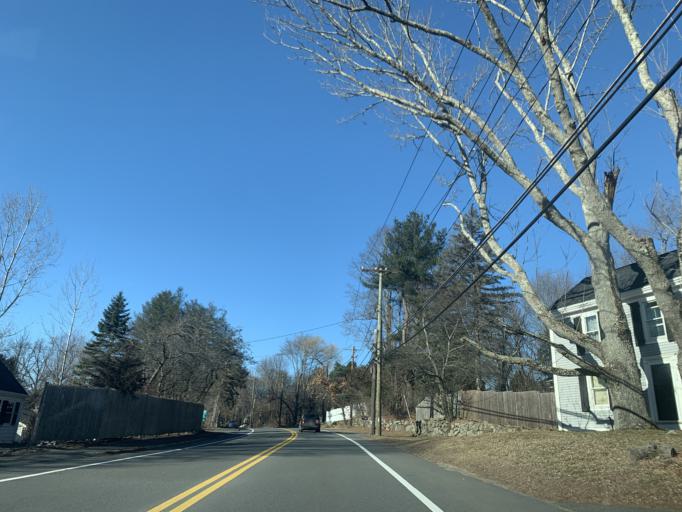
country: US
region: Massachusetts
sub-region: Middlesex County
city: Wayland
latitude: 42.3616
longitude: -71.3476
